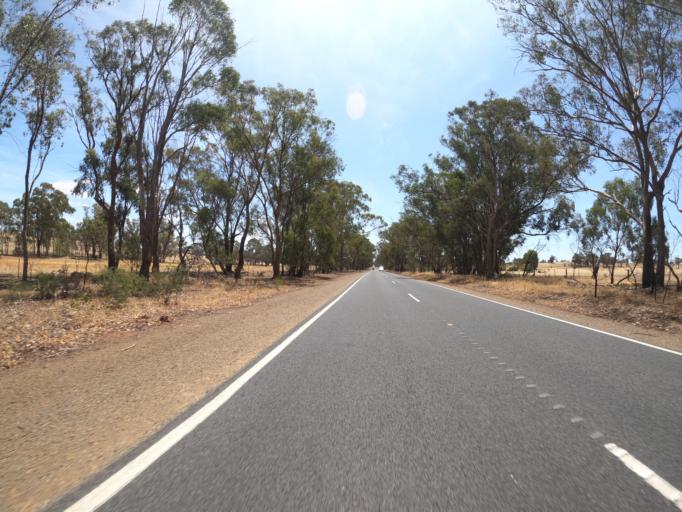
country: AU
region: Victoria
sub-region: Benalla
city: Benalla
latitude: -36.3678
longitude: 145.9709
